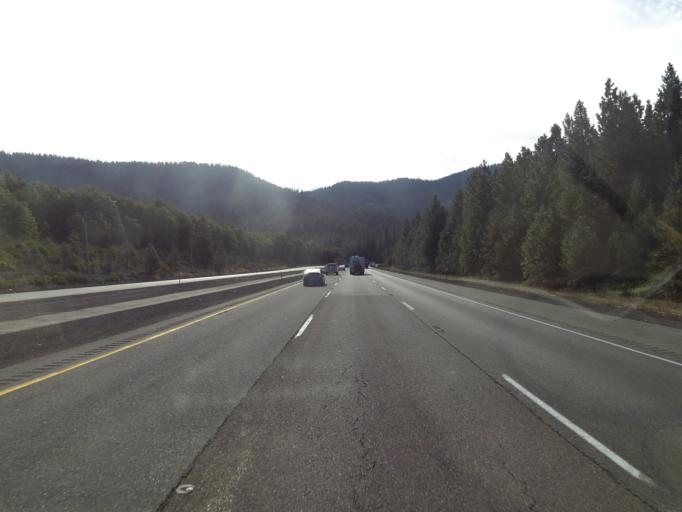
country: US
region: California
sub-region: Siskiyou County
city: Dunsmuir
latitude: 41.2531
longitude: -122.2635
